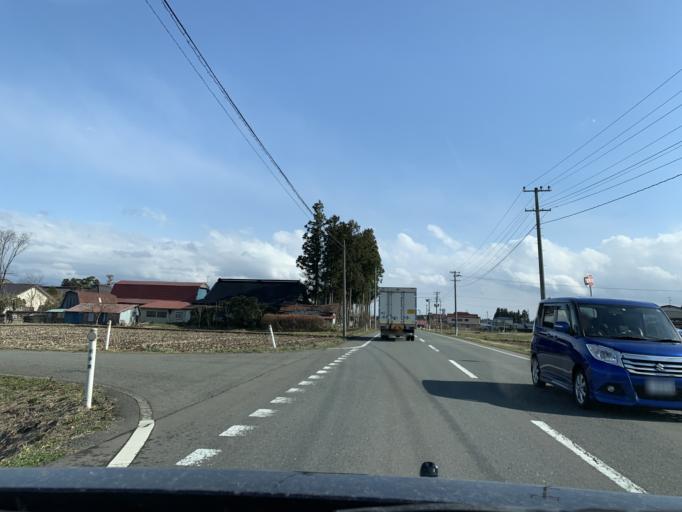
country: JP
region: Iwate
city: Mizusawa
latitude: 39.1329
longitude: 141.0526
